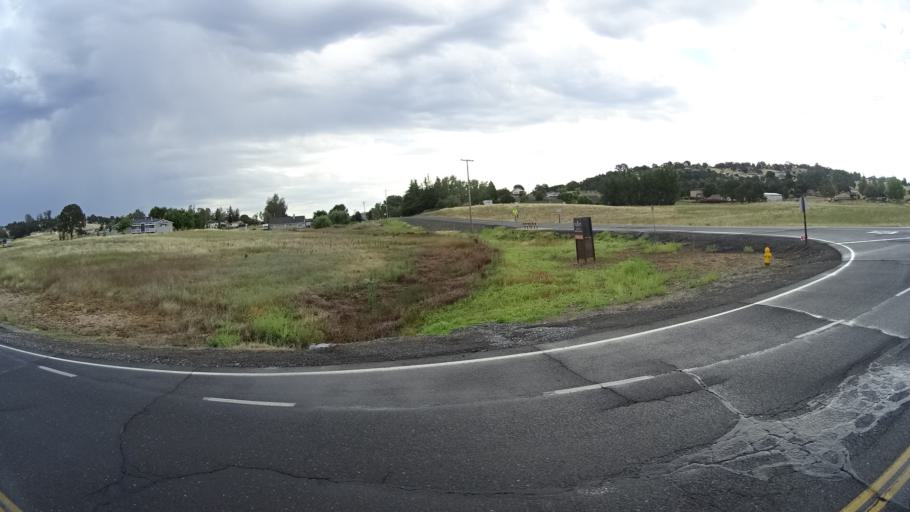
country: US
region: California
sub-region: Calaveras County
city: Copperopolis
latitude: 37.9320
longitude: -120.6433
